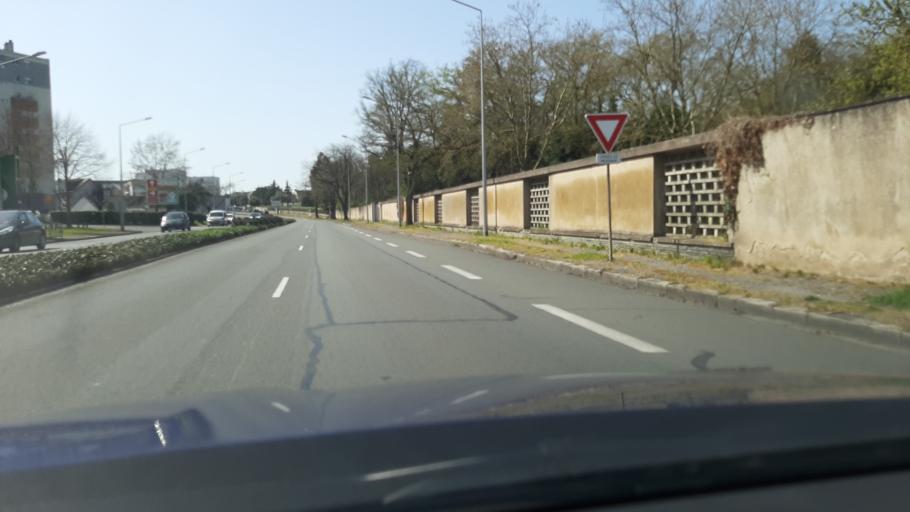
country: FR
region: Pays de la Loire
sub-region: Departement de Maine-et-Loire
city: Angers
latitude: 47.4579
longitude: -0.5256
